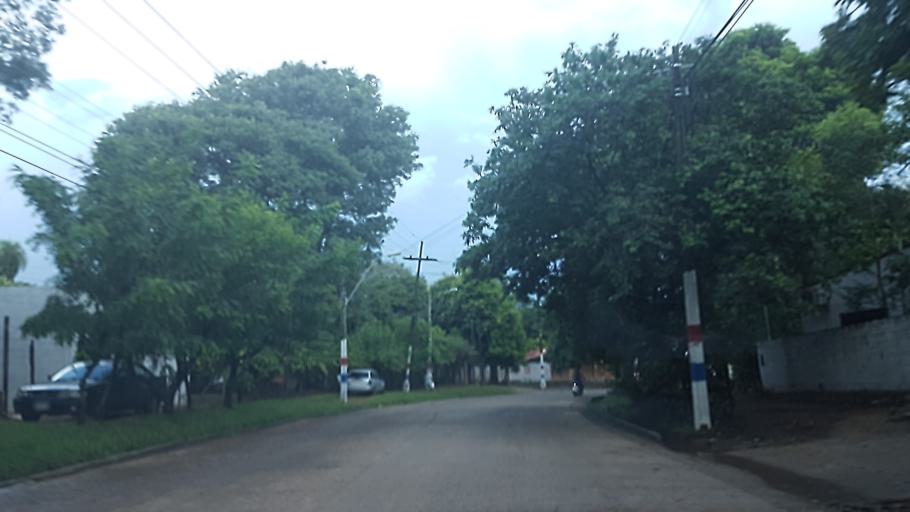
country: PY
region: Central
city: Colonia Mariano Roque Alonso
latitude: -25.1981
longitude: -57.5351
